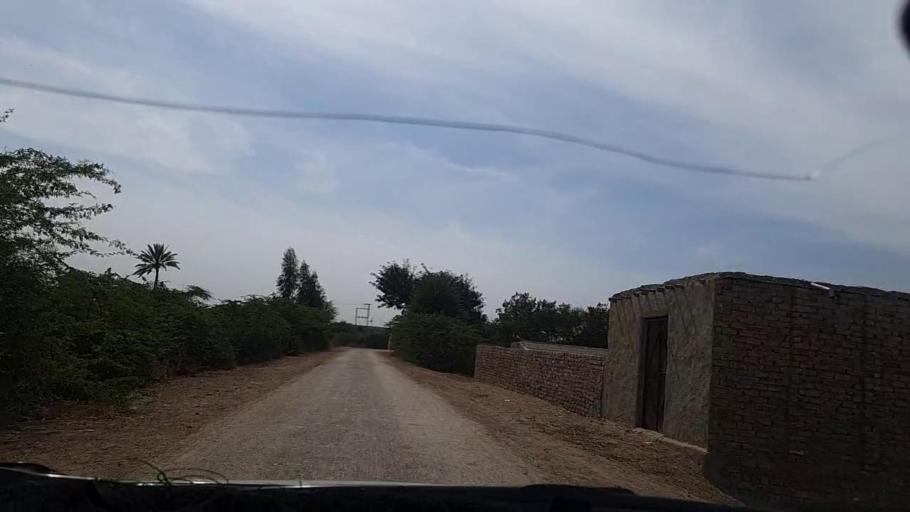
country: PK
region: Sindh
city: Dhoro Naro
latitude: 25.4369
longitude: 69.5082
